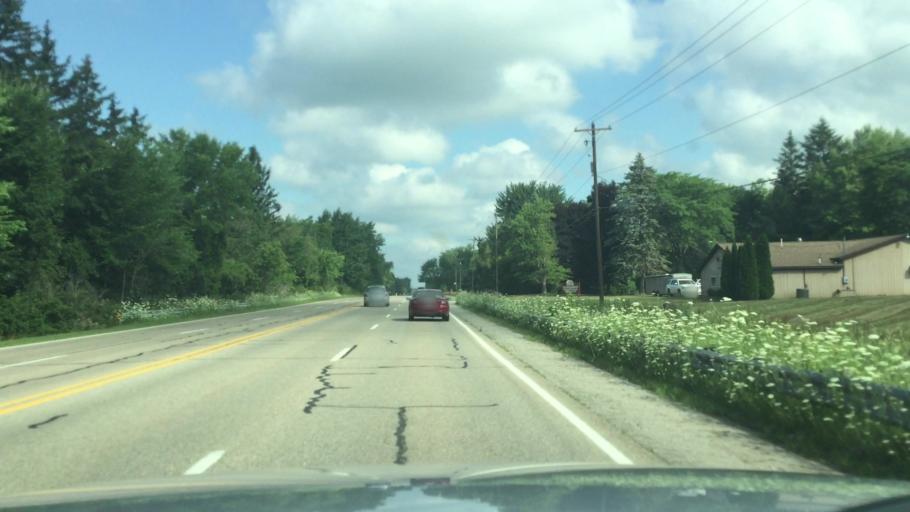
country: US
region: Michigan
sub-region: Genesee County
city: Clio
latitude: 43.2181
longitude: -83.7451
